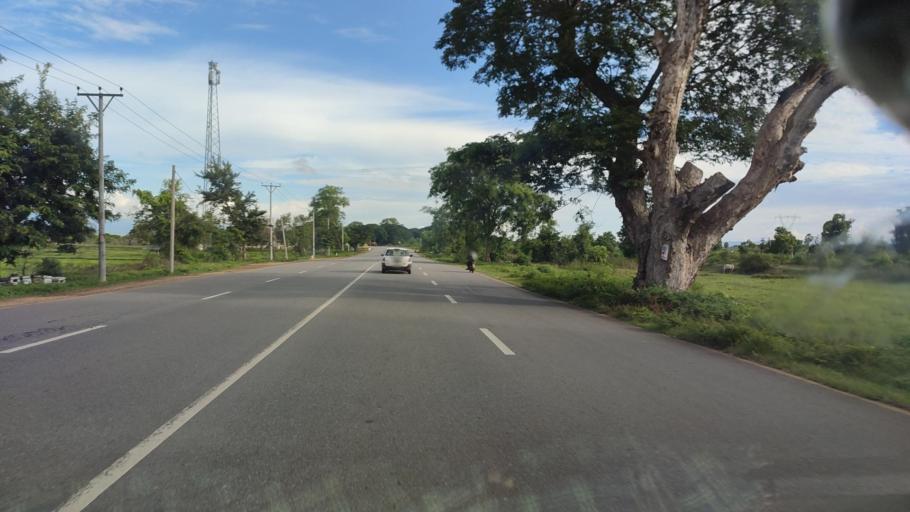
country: MM
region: Mandalay
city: Yamethin
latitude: 20.1962
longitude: 96.1831
